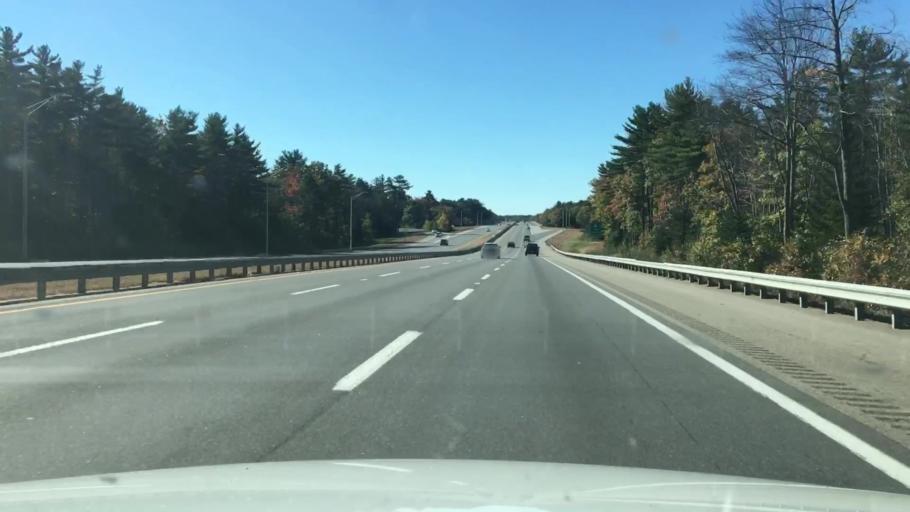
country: US
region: Maine
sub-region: York County
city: Wells Beach Station
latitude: 43.3310
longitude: -70.6041
